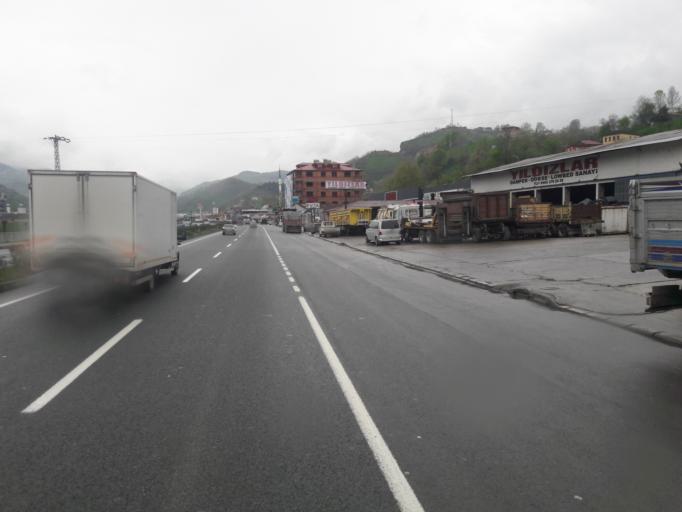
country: TR
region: Trabzon
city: Caglayan
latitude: 40.9373
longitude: 39.7333
